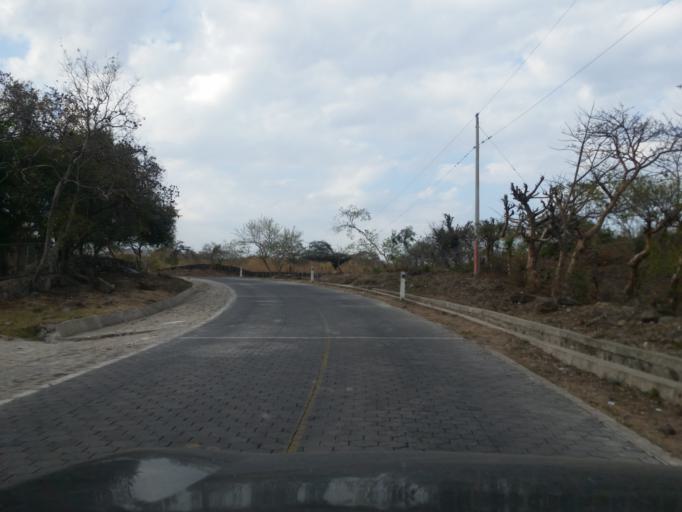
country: NI
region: Jinotega
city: La Concordia
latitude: 13.1833
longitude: -86.1691
